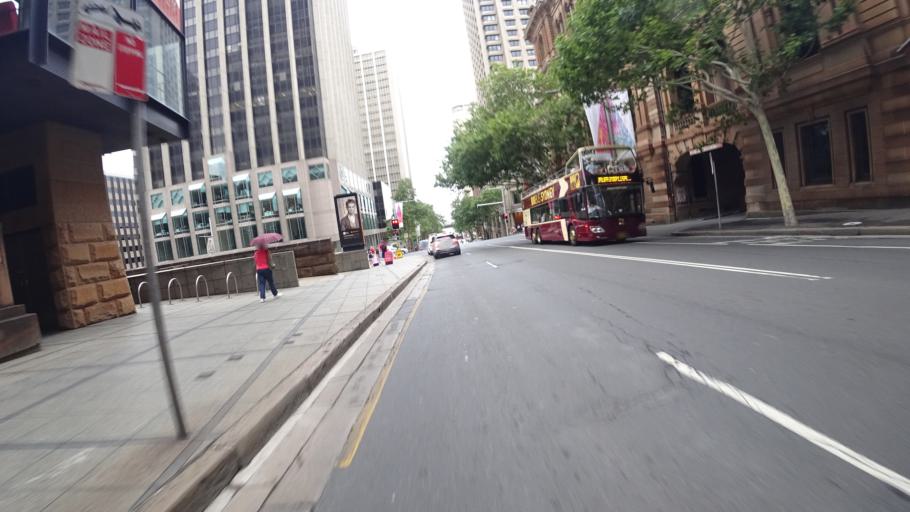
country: AU
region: New South Wales
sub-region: City of Sydney
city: Sydney
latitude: -33.8641
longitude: 151.2117
